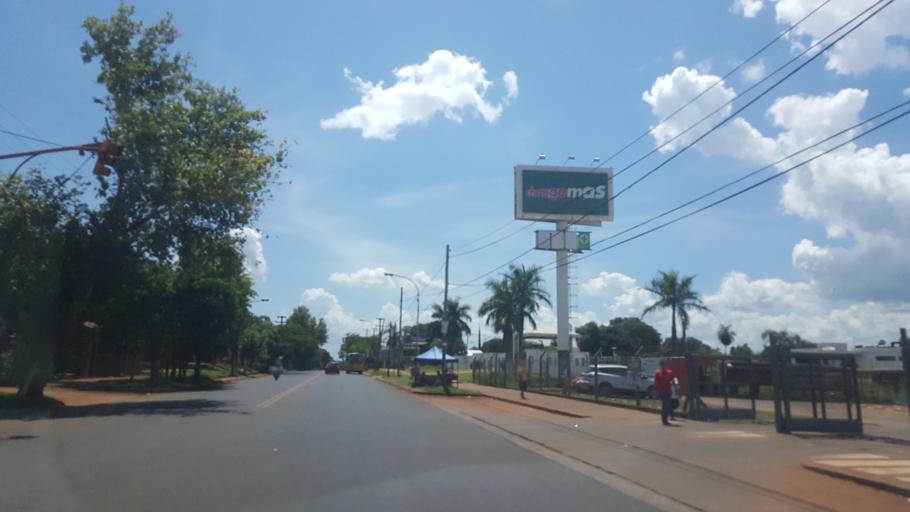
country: AR
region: Misiones
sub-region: Departamento de Capital
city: Posadas
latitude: -27.3678
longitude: -55.9265
